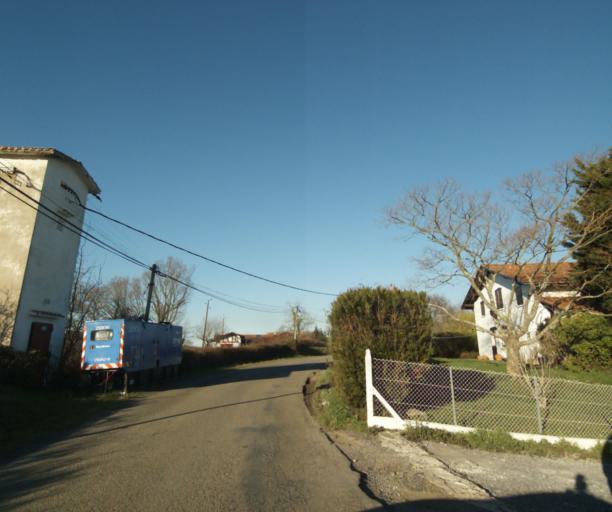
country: FR
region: Aquitaine
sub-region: Departement des Pyrenees-Atlantiques
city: Urrugne
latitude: 43.3502
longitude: -1.7122
